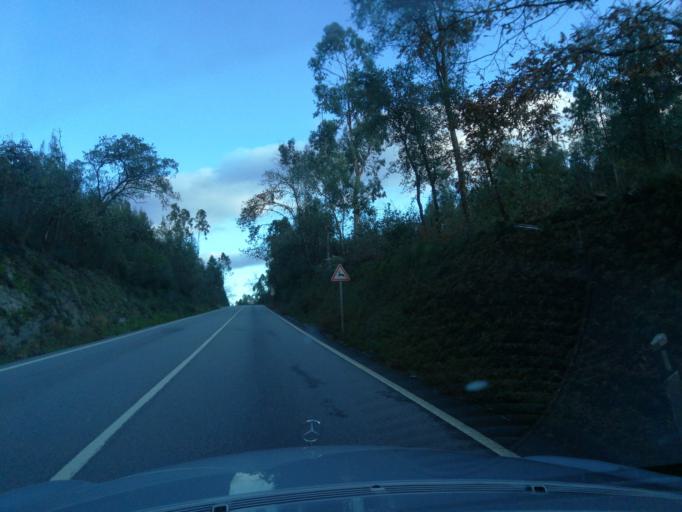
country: PT
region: Braga
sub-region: Barcelos
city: Vila Frescainha
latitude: 41.5688
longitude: -8.6820
